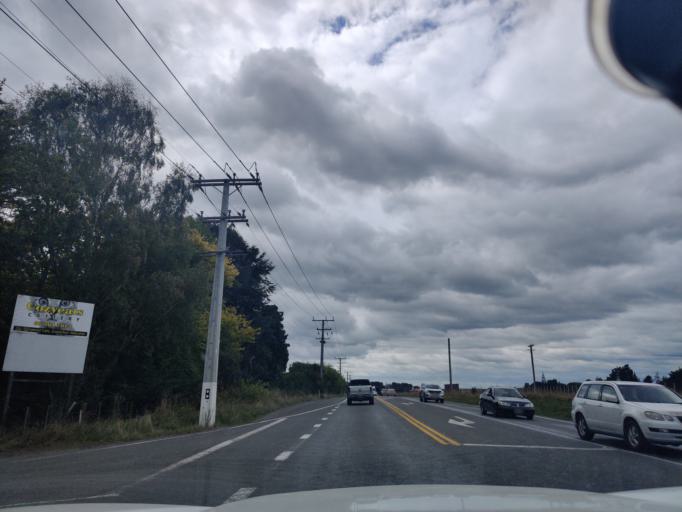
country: NZ
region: Wellington
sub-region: Kapiti Coast District
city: Otaki
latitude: -40.7470
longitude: 175.1676
